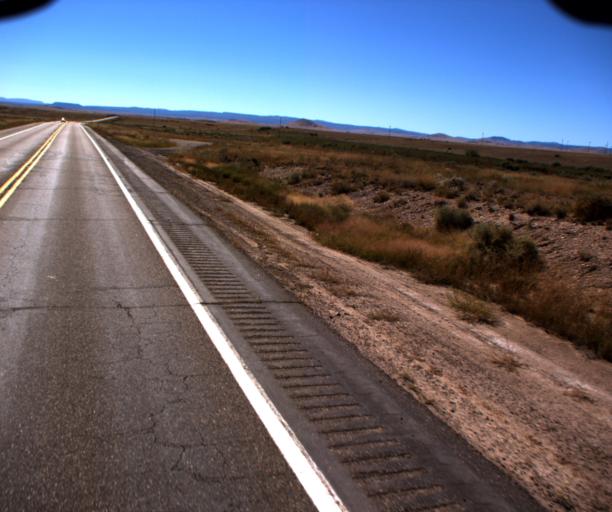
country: US
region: Arizona
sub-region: Apache County
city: Saint Johns
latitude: 34.3262
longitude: -109.3859
